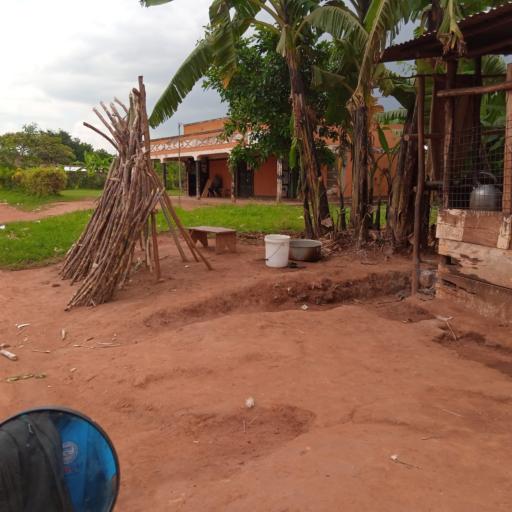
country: UG
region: Eastern Region
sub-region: Mbale District
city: Mbale
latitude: 1.1240
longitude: 34.1837
